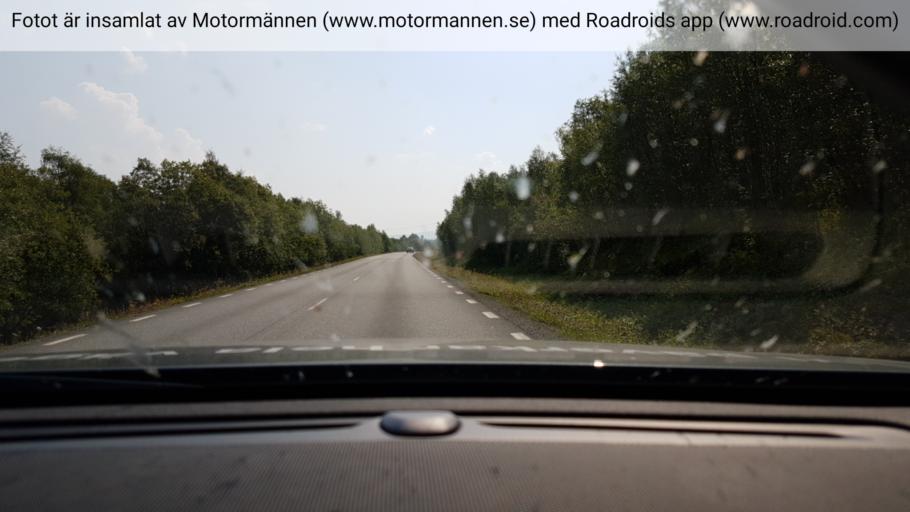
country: NO
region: Nordland
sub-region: Rana
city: Mo i Rana
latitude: 65.7221
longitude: 15.1888
